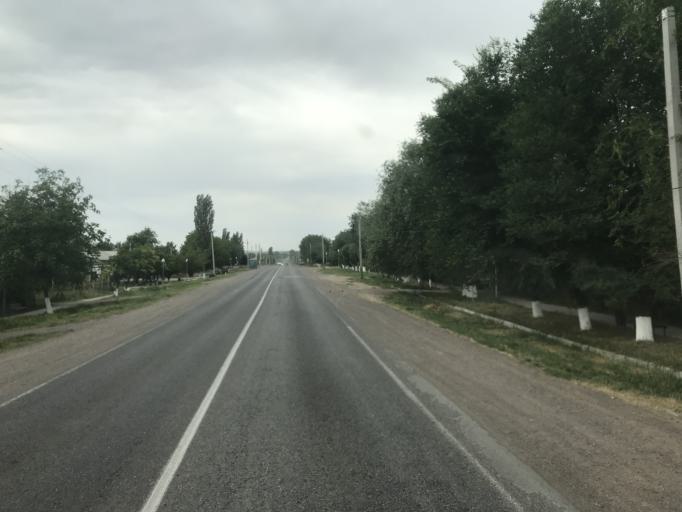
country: UZ
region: Toshkent
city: Salor
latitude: 41.4938
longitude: 69.3168
